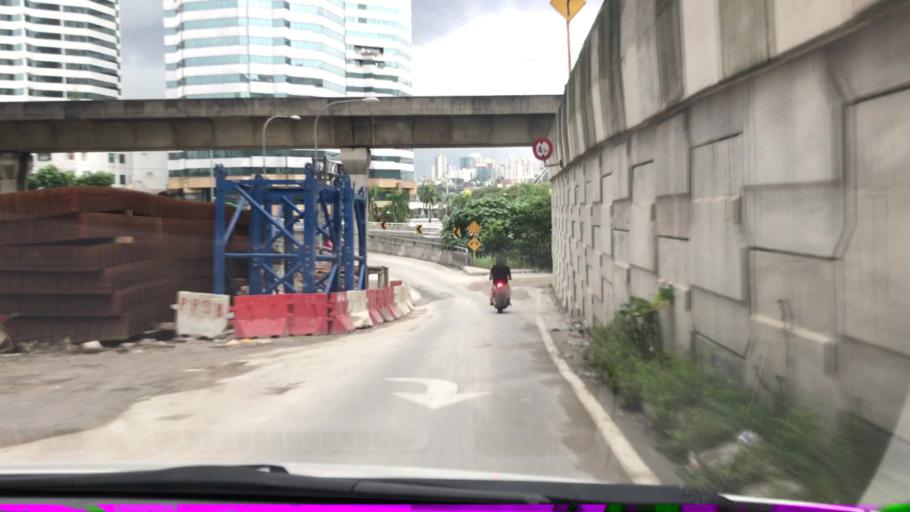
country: MY
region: Kuala Lumpur
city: Kuala Lumpur
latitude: 3.1141
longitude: 101.6642
